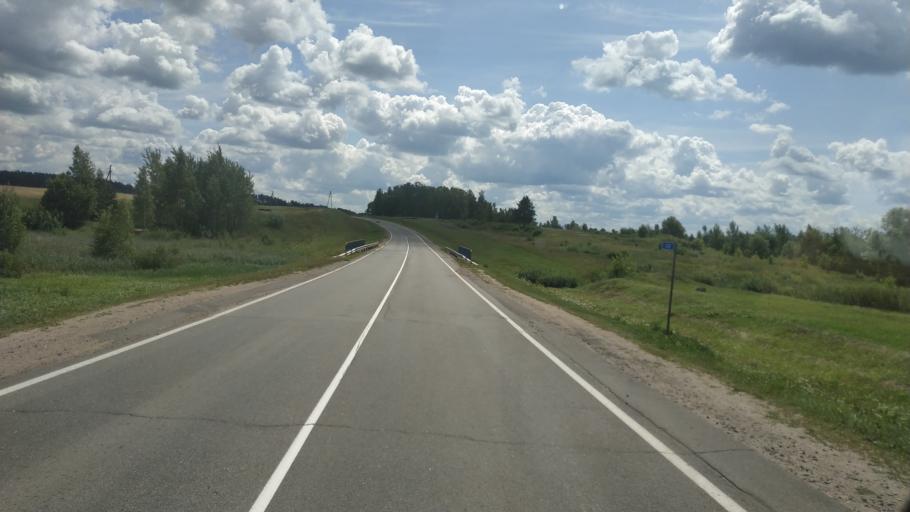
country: BY
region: Mogilev
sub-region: Mahilyowski Rayon
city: Veyno
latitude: 53.8362
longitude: 30.3996
